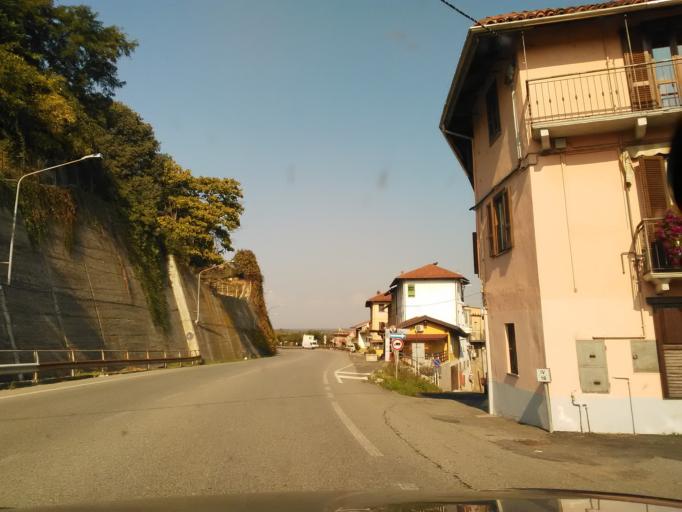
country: IT
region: Piedmont
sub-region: Provincia di Biella
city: Salussola
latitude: 45.4469
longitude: 8.1125
